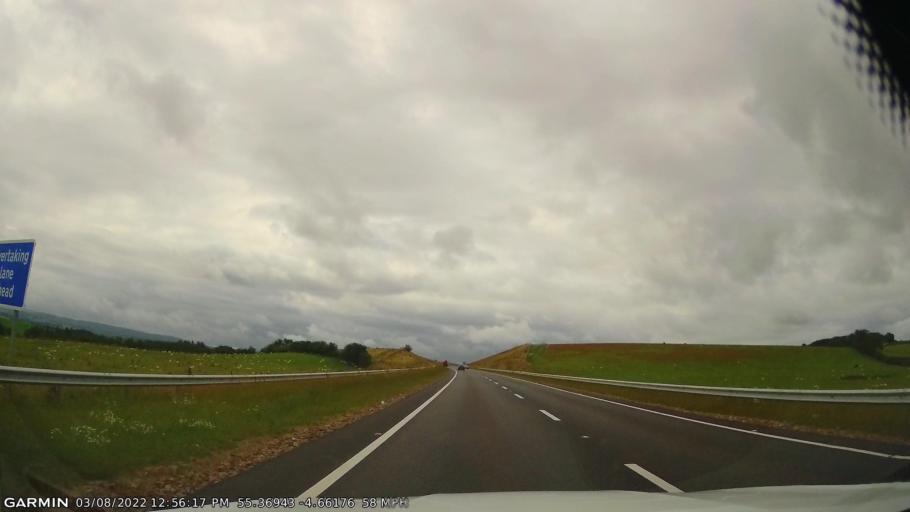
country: GB
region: Scotland
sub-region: South Ayrshire
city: Maybole
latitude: 55.3694
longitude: -4.6616
